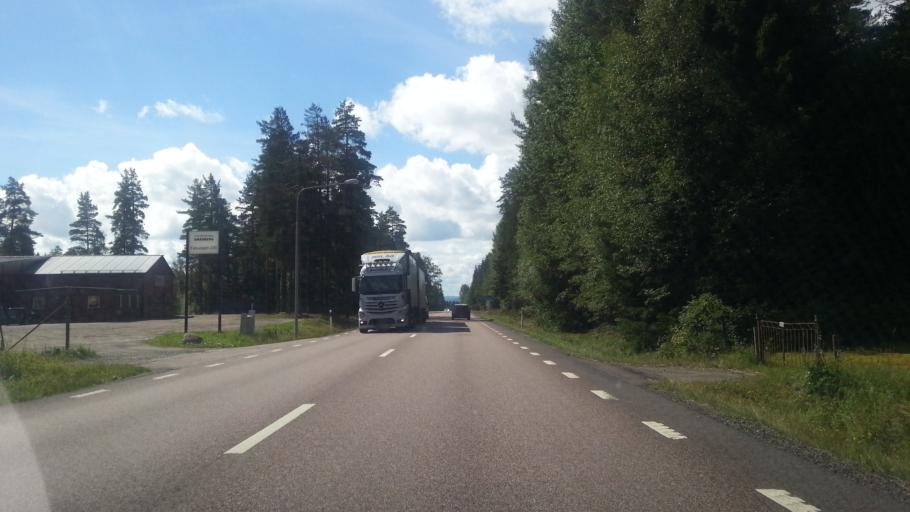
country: SE
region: Dalarna
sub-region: Ludvika Kommun
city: Ludvika
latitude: 60.2243
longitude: 15.2293
